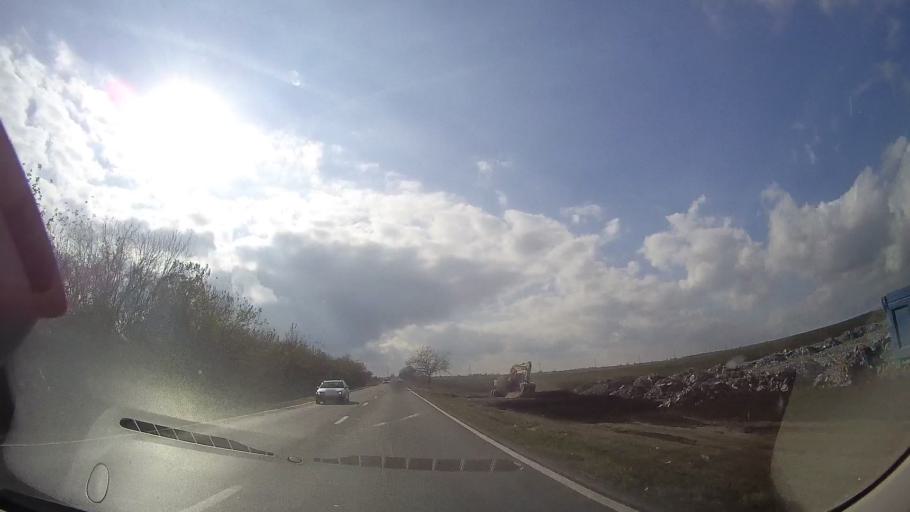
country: RO
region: Constanta
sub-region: Comuna Agigea
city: Agigea
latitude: 44.0815
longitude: 28.6045
